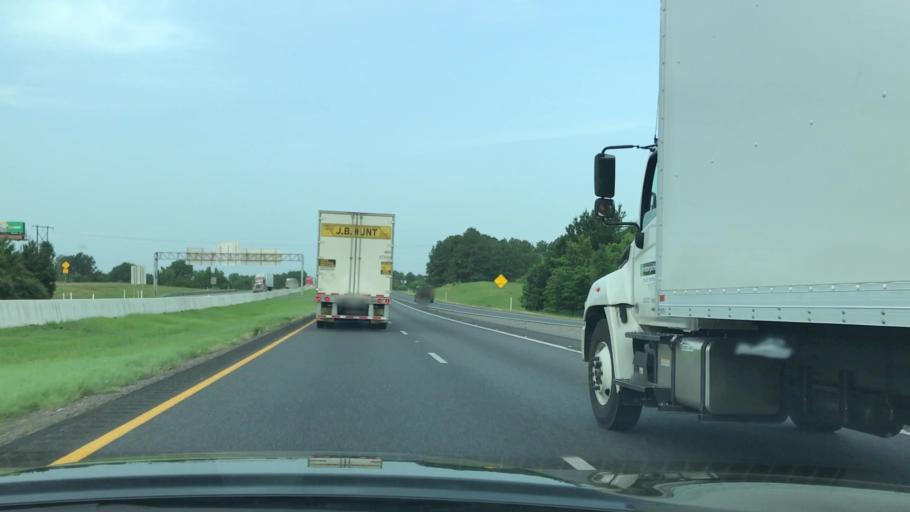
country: US
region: Texas
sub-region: Gregg County
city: Longview
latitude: 32.4451
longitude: -94.7233
